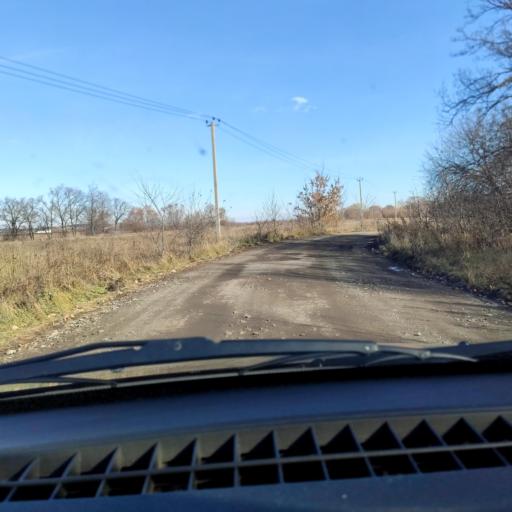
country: RU
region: Bashkortostan
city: Avdon
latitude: 54.4955
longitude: 55.8597
